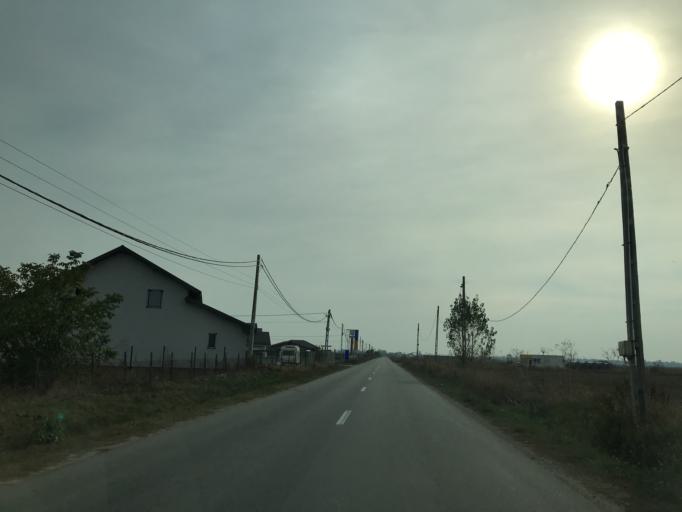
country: RO
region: Olt
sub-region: Comuna Slatioara
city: Slatioara
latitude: 44.3935
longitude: 24.3238
